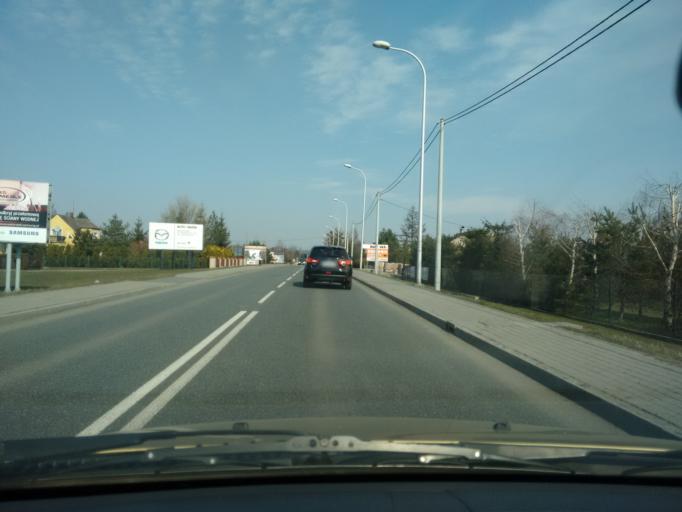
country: PL
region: Silesian Voivodeship
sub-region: Powiat cieszynski
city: Zamarski
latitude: 49.7559
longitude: 18.6789
